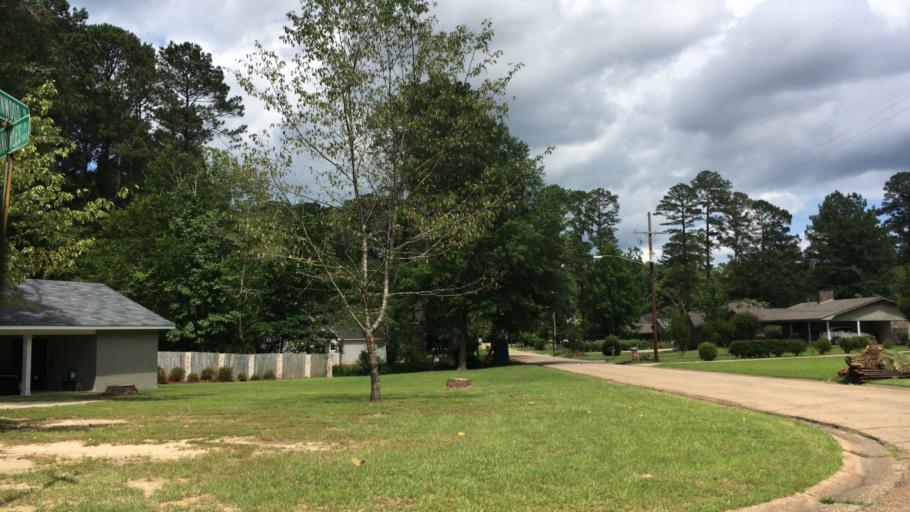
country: US
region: Louisiana
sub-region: Lincoln Parish
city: Ruston
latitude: 32.5481
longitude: -92.6380
